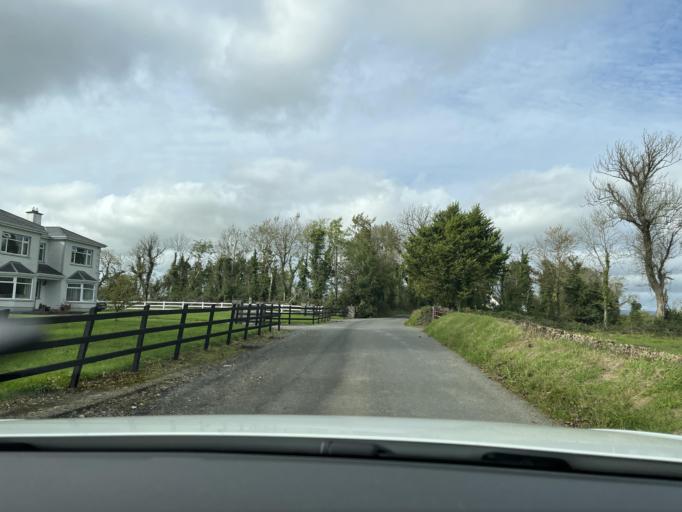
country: IE
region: Connaught
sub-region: County Leitrim
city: Carrick-on-Shannon
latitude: 53.9582
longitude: -8.0687
